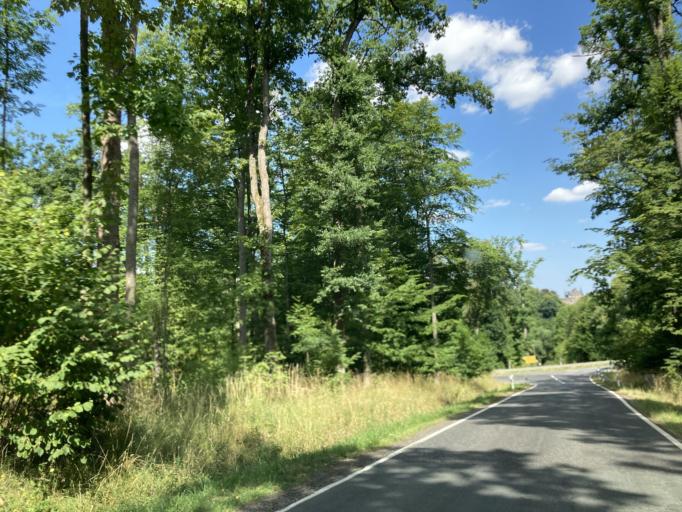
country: DE
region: Hesse
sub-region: Regierungsbezirk Giessen
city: Lauterbach
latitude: 50.5964
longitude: 9.3905
